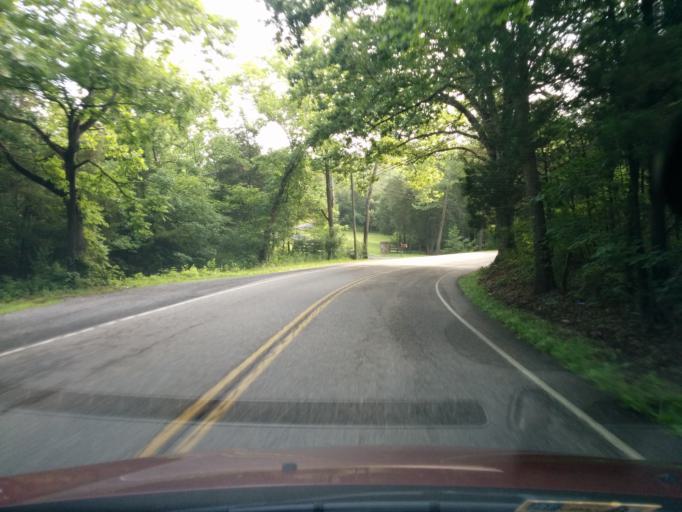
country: US
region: Virginia
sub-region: City of Lexington
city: Lexington
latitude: 37.7498
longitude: -79.5013
